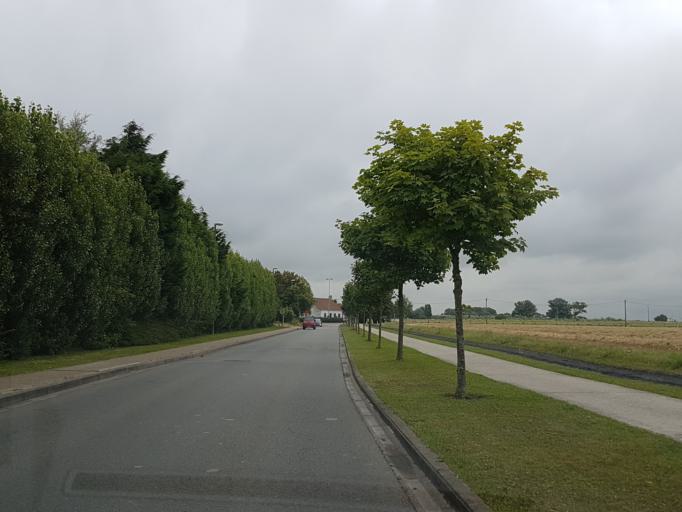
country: BE
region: Flanders
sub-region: Provincie West-Vlaanderen
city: Bredene
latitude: 51.2446
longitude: 2.9844
